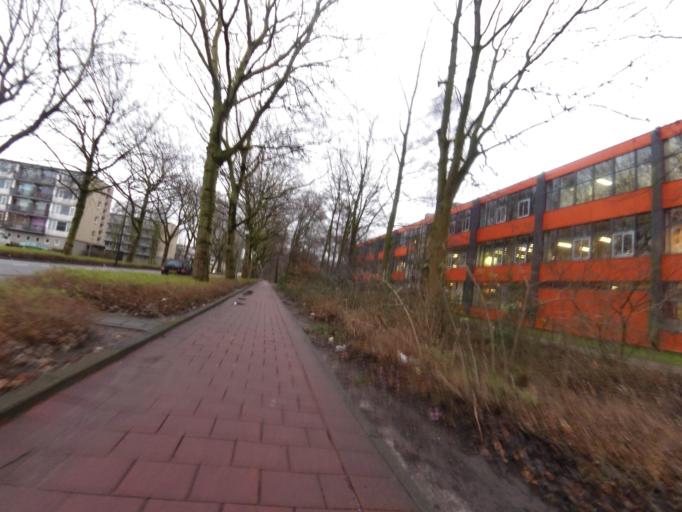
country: NL
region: South Holland
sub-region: Gemeente Vlaardingen
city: Vlaardingen
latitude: 51.9047
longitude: 4.3159
